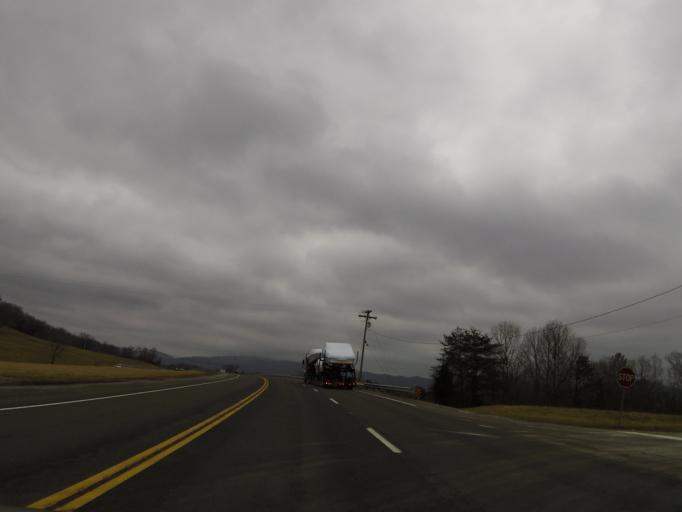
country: US
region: Tennessee
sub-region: Scott County
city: Huntsville
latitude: 36.3798
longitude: -84.4069
